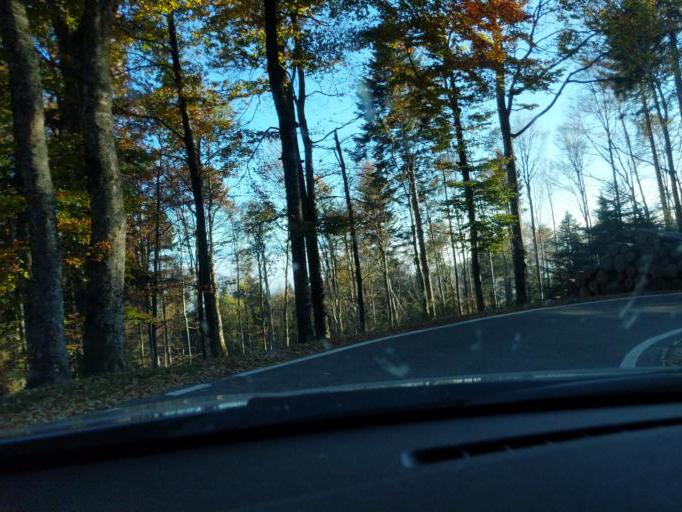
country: CH
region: Neuchatel
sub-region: Neuchatel District
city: Le Landeron
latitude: 47.1140
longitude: 7.0486
